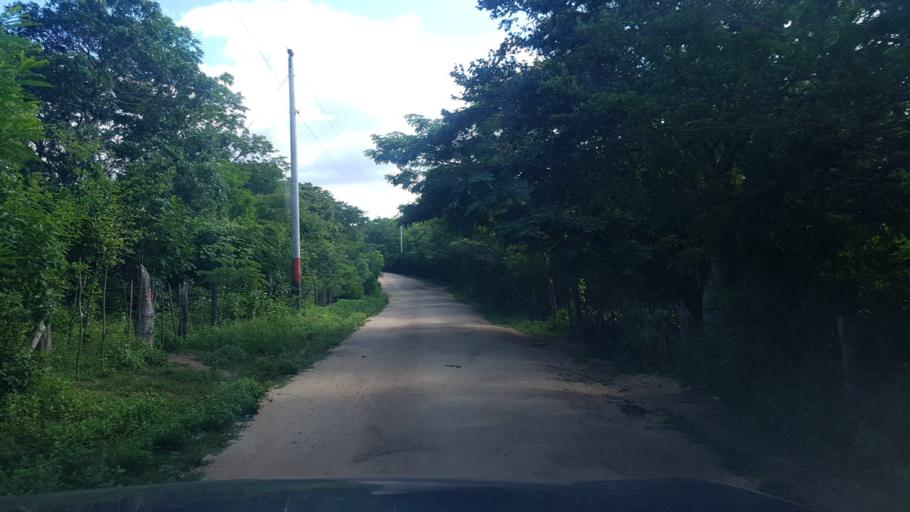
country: NI
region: Nueva Segovia
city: Mozonte
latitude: 13.6538
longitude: -86.3982
